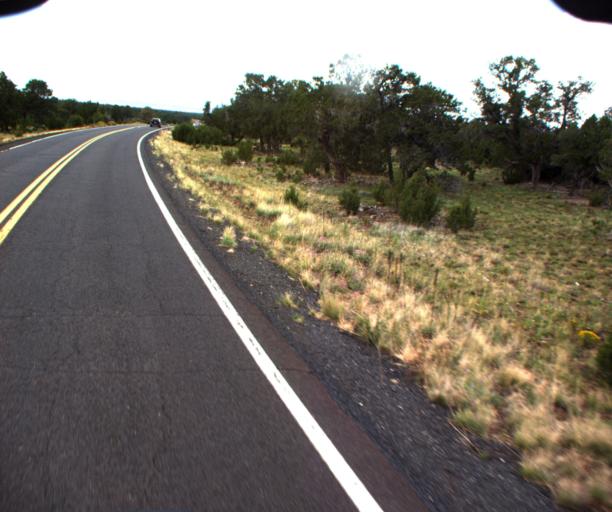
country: US
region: Arizona
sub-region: Coconino County
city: Parks
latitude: 35.5337
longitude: -111.8508
